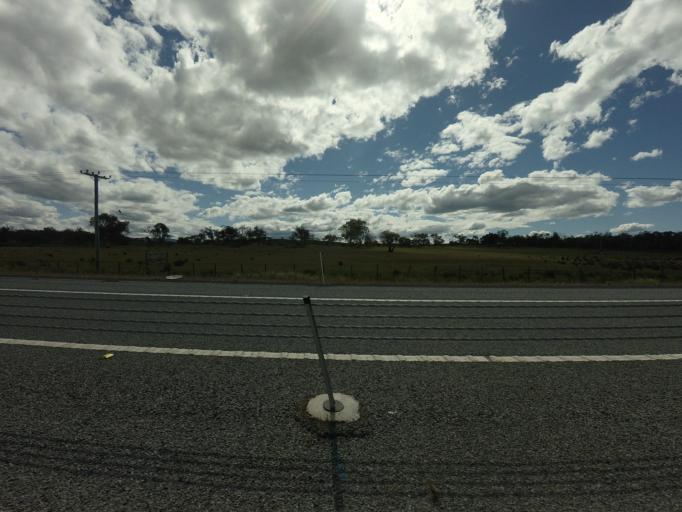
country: AU
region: Tasmania
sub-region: Northern Midlands
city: Evandale
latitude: -42.0766
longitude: 147.4575
